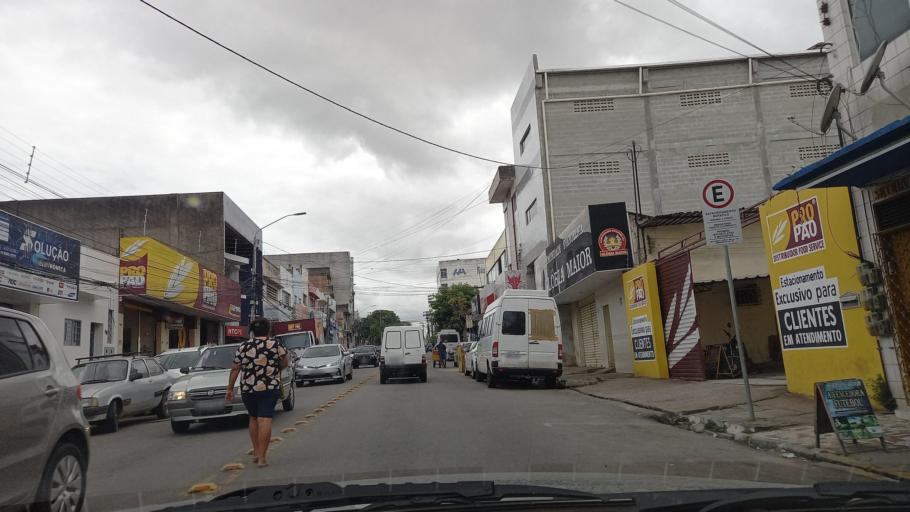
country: BR
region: Pernambuco
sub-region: Caruaru
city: Caruaru
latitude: -8.2818
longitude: -35.9722
